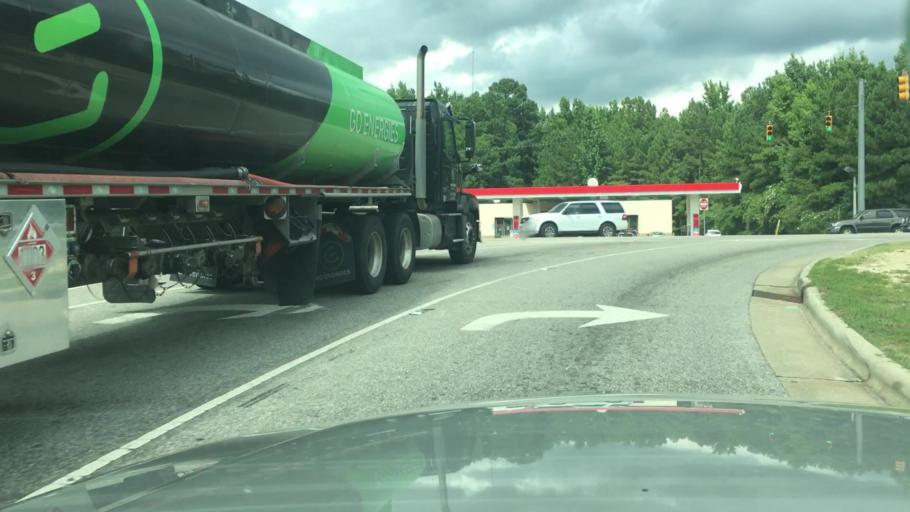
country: US
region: North Carolina
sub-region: Cumberland County
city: Hope Mills
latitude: 35.0030
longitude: -78.9794
